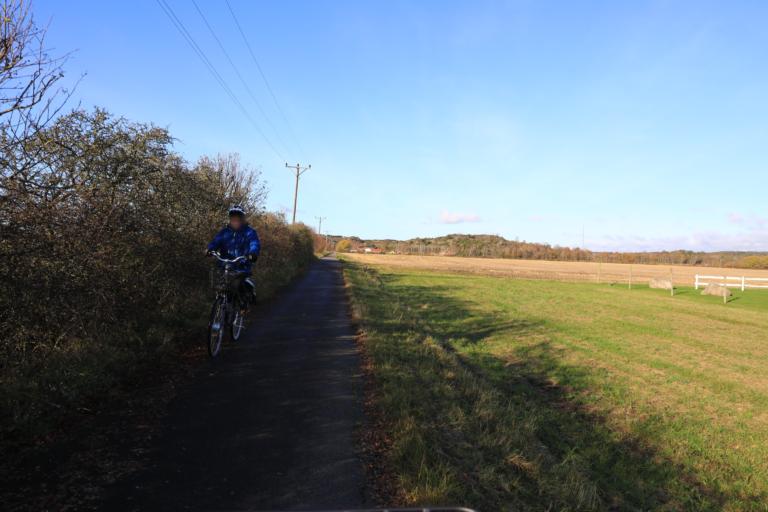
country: SE
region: Halland
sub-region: Varbergs Kommun
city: Varberg
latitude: 57.1495
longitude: 12.2467
